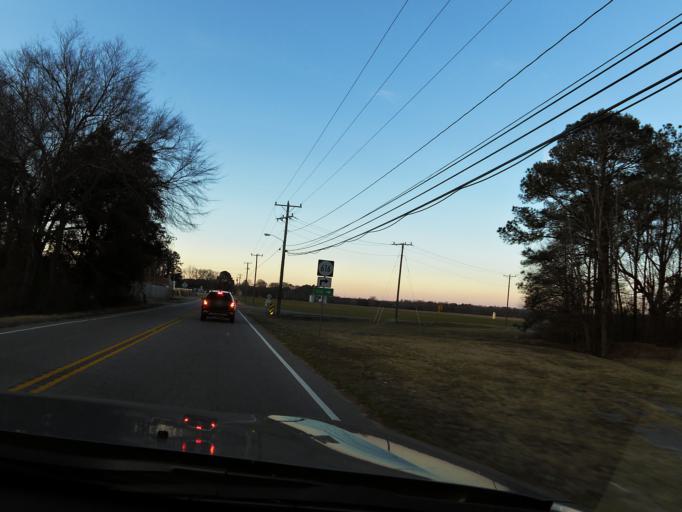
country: US
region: Virginia
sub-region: Southampton County
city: Courtland
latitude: 36.7263
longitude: -77.0718
